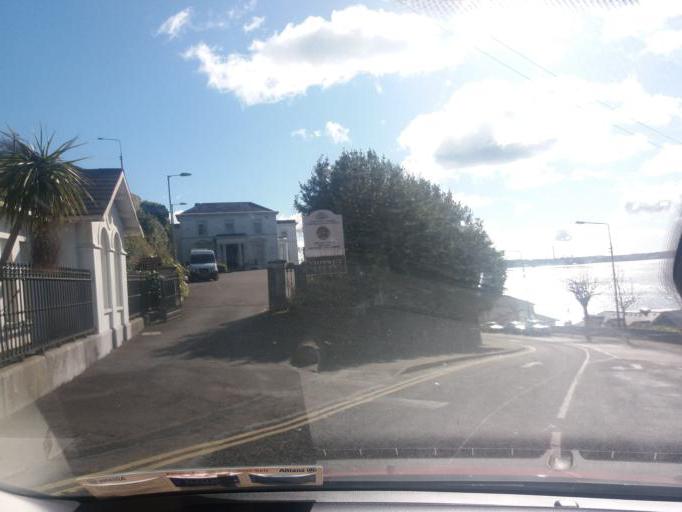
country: IE
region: Munster
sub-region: County Cork
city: Cobh
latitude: 51.8494
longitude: -8.2989
